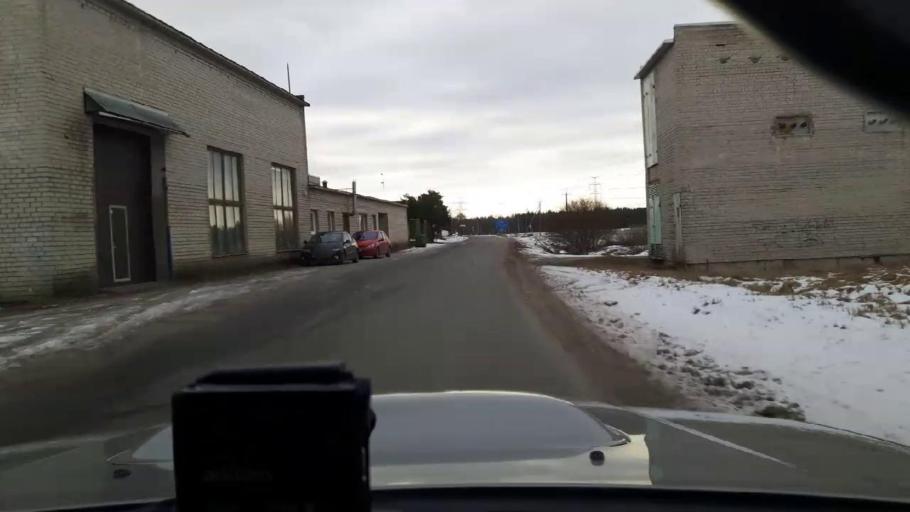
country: EE
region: Harju
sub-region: Saue vald
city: Laagri
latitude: 59.3494
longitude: 24.5994
